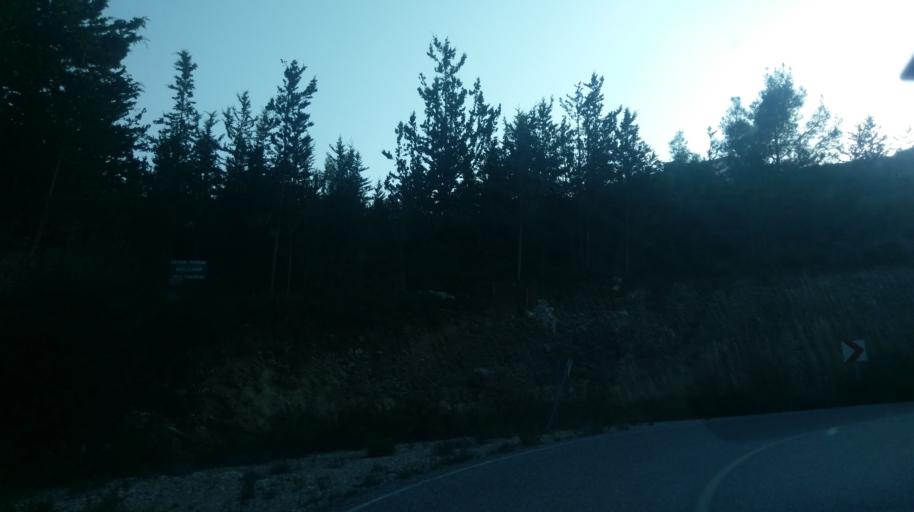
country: CY
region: Ammochostos
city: Trikomo
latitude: 35.4048
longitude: 33.9043
